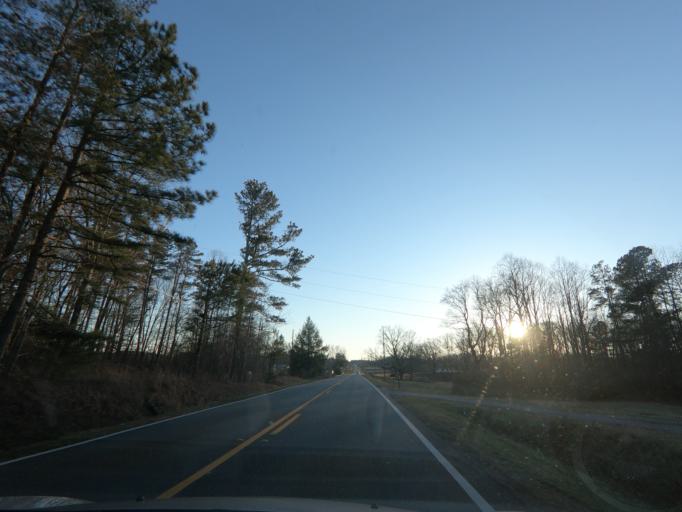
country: US
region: Georgia
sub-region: Dawson County
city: Dawsonville
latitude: 34.3230
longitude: -84.1366
